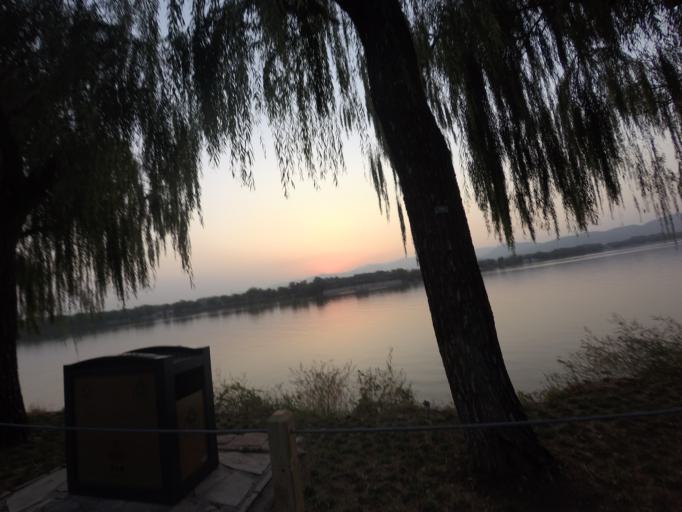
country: CN
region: Beijing
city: Haidian
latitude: 39.9849
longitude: 116.2717
